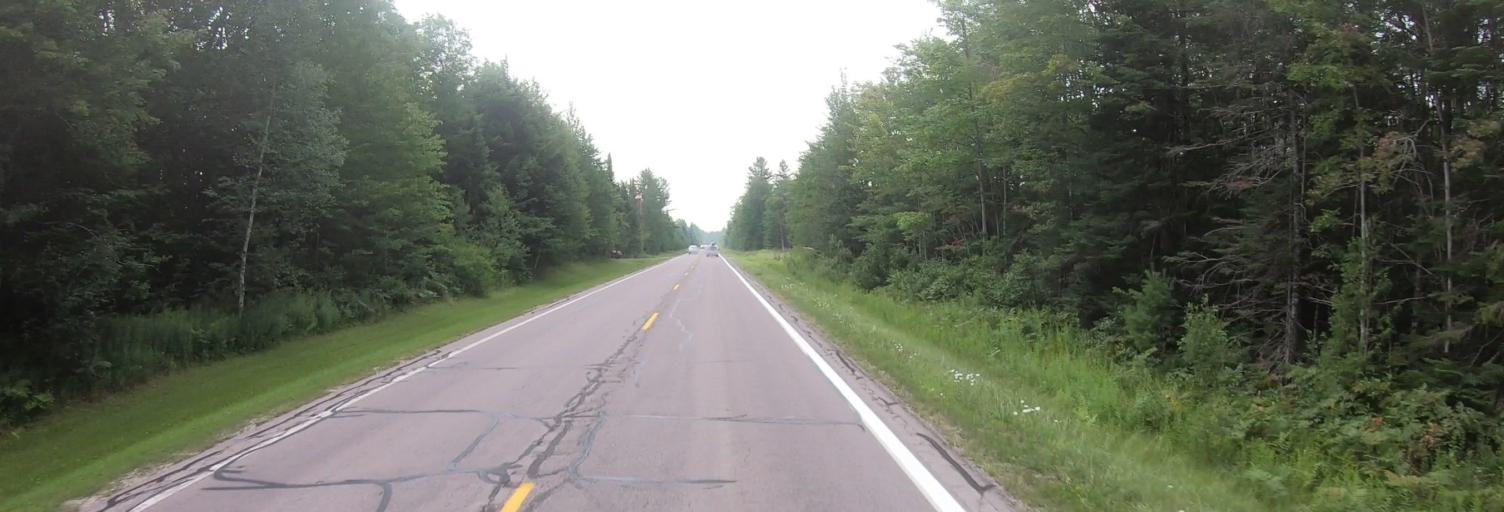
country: US
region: Michigan
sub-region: Luce County
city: Newberry
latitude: 46.4817
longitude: -85.4269
